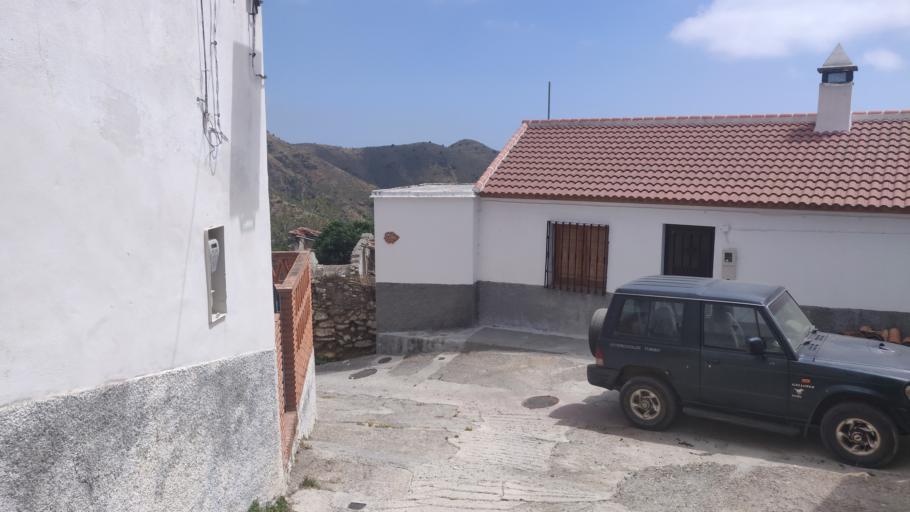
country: ES
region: Andalusia
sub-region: Provincia de Granada
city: Rubite
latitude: 36.8080
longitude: -3.3483
